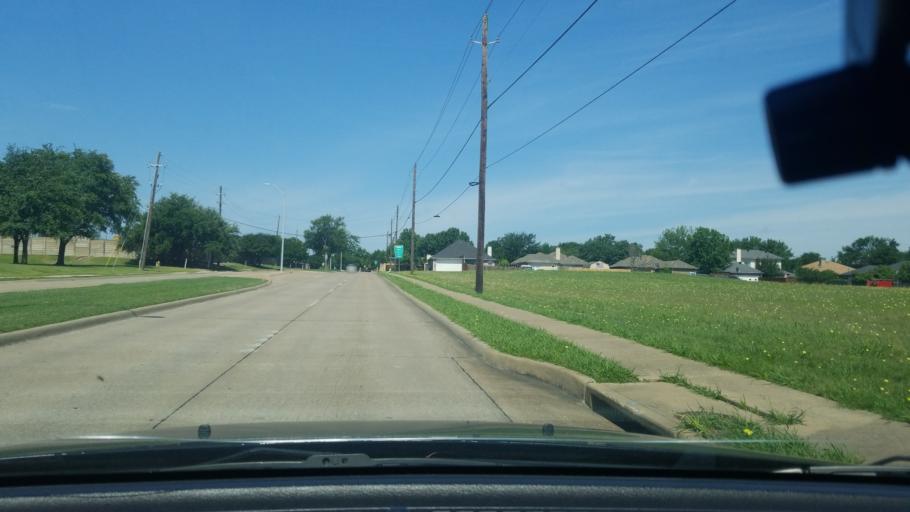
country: US
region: Texas
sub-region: Dallas County
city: Mesquite
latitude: 32.7704
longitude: -96.5835
